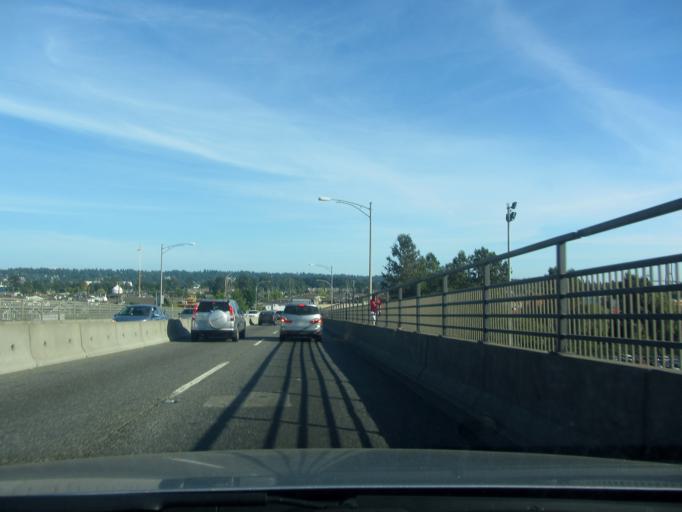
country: CA
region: British Columbia
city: New Westminster
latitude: 49.1931
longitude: -122.9437
